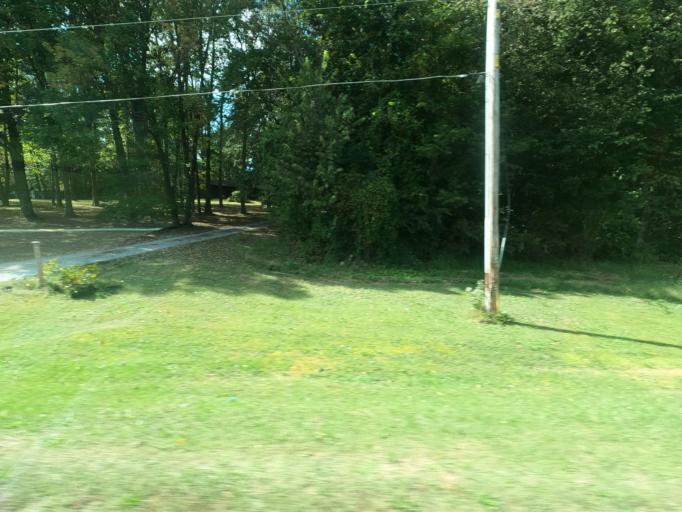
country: US
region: Illinois
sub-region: Johnson County
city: Vienna
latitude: 37.4285
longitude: -88.8929
